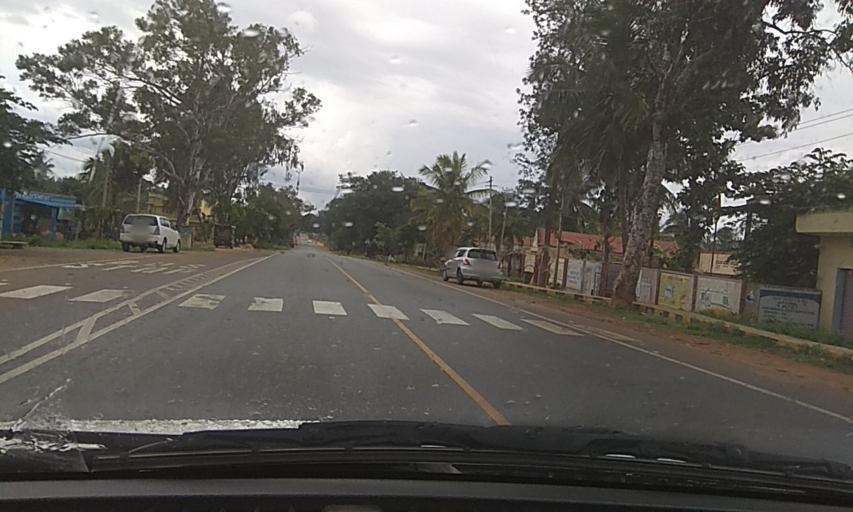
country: IN
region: Karnataka
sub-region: Tumkur
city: Kunigal
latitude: 12.9414
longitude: 77.0282
